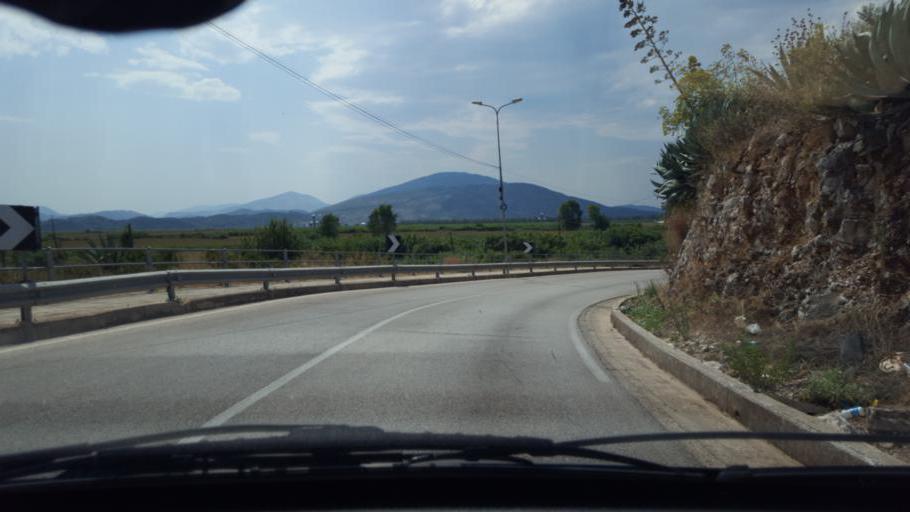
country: AL
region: Vlore
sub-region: Rrethi i Sarandes
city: Sarande
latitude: 39.8380
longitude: 20.0239
